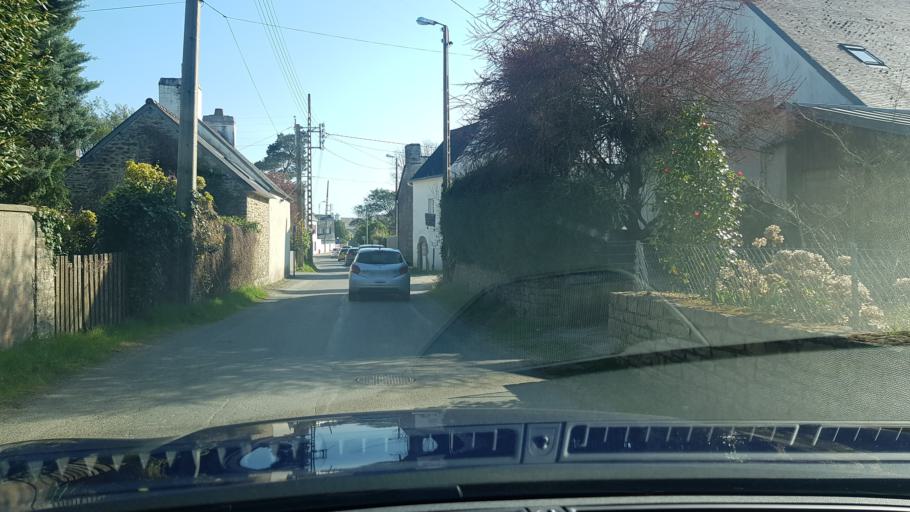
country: FR
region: Brittany
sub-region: Departement du Finistere
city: Clohars-Carnoet
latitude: 47.7772
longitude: -3.6093
